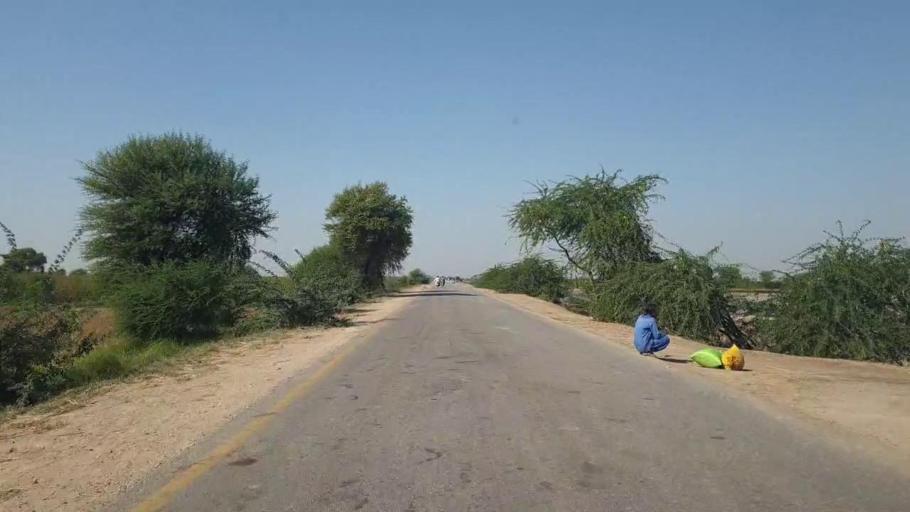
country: PK
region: Sindh
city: Rajo Khanani
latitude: 25.0117
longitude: 68.8331
